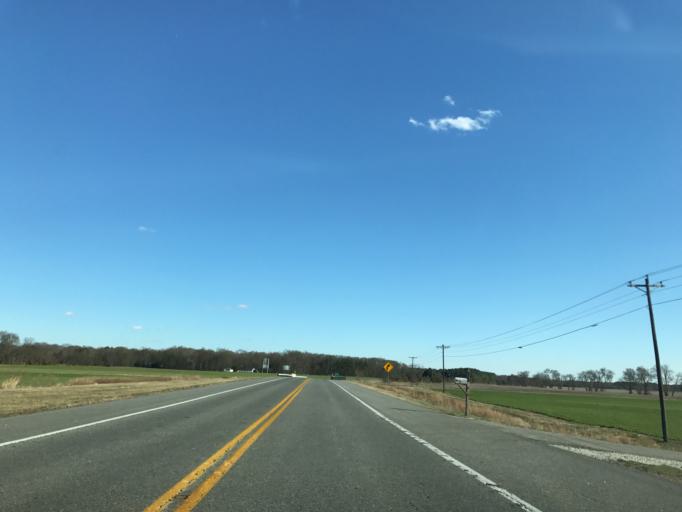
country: US
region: Maryland
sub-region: Caroline County
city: Greensboro
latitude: 39.0692
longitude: -75.8547
